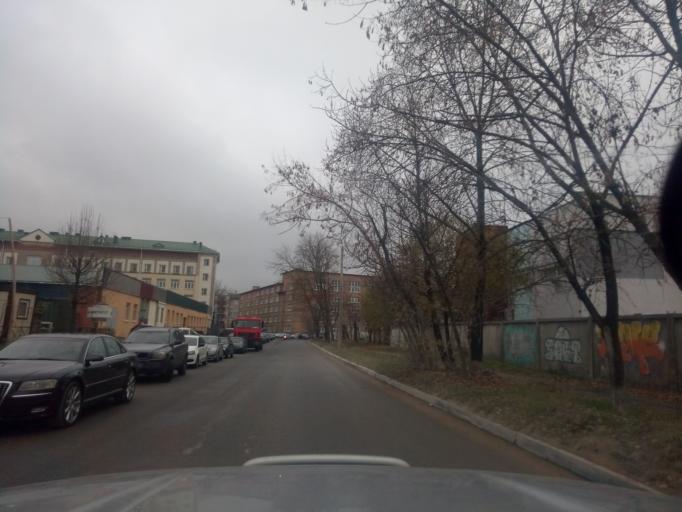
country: BY
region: Minsk
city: Minsk
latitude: 53.9066
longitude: 27.6002
